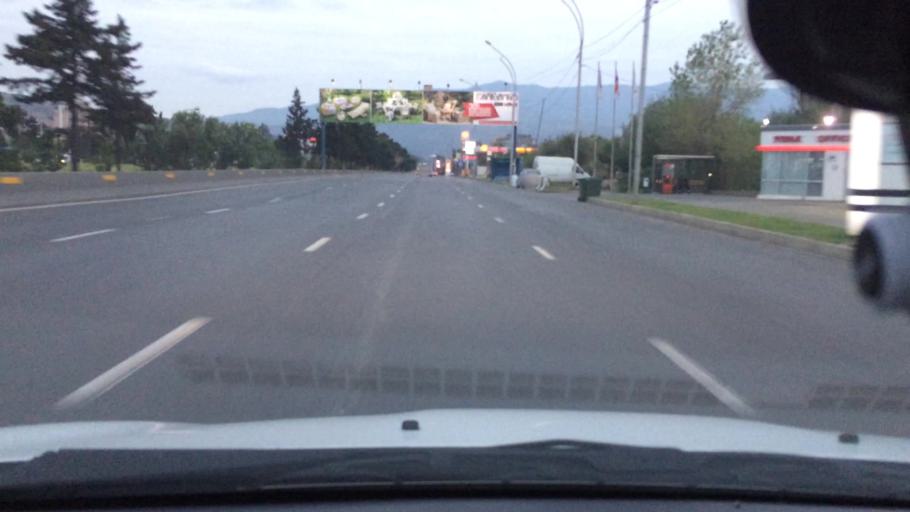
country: GE
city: Zahesi
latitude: 41.7835
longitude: 44.7698
